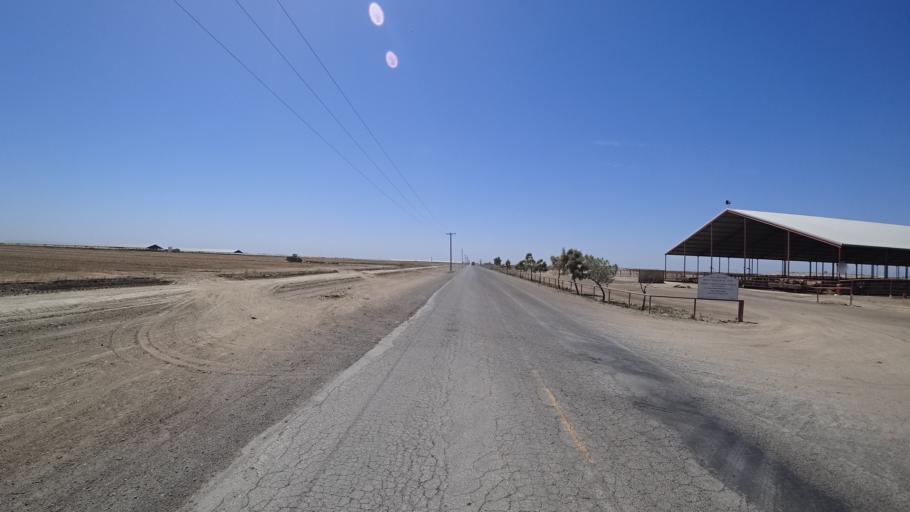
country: US
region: California
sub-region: Kings County
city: Armona
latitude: 36.2054
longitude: -119.6907
